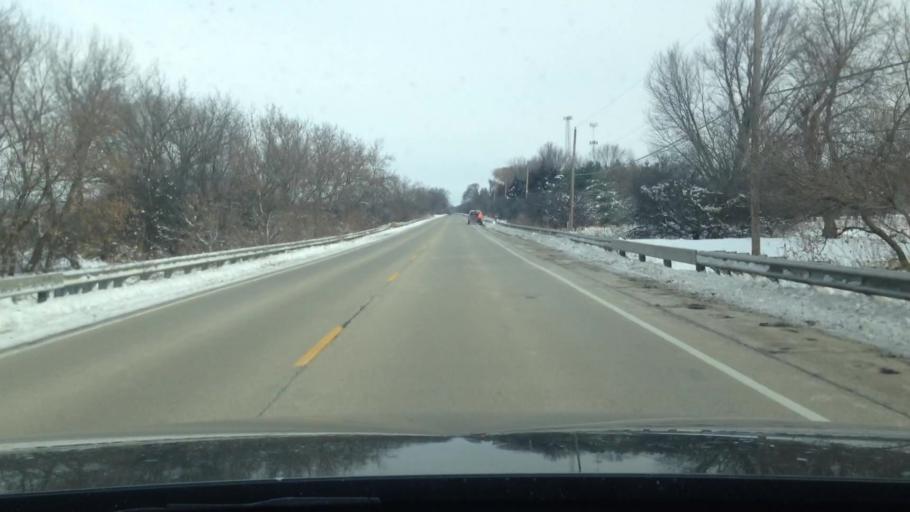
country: US
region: Illinois
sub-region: McHenry County
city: Woodstock
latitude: 42.3696
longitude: -88.4431
